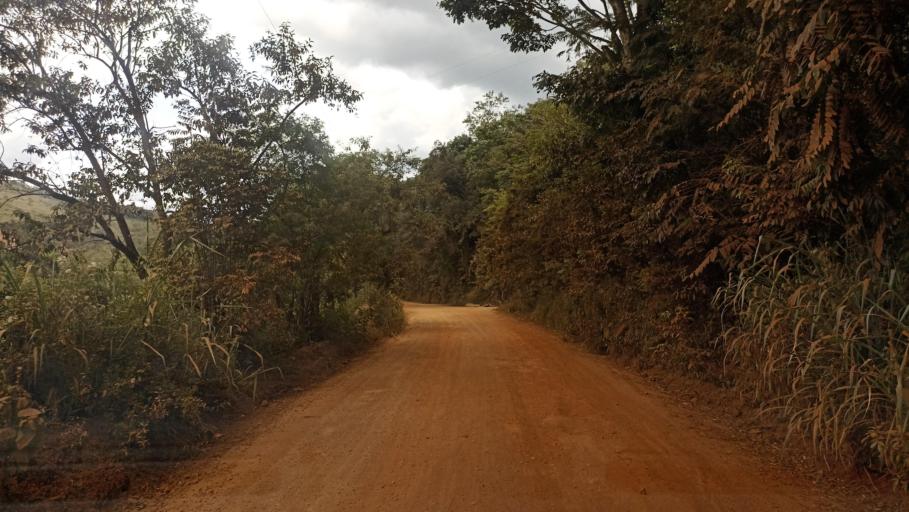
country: BR
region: Minas Gerais
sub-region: Itabirito
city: Itabirito
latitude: -20.3567
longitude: -43.7703
